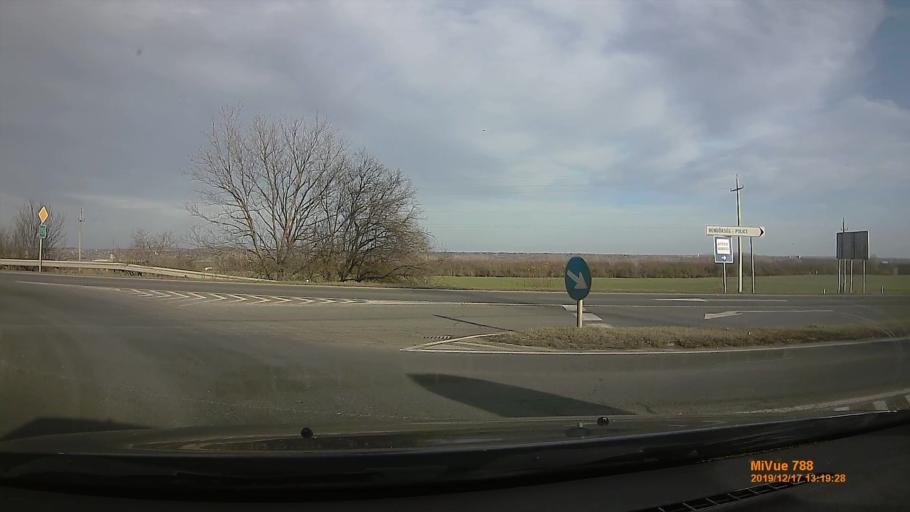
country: HU
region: Fejer
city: Lepseny
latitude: 46.9899
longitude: 18.1889
